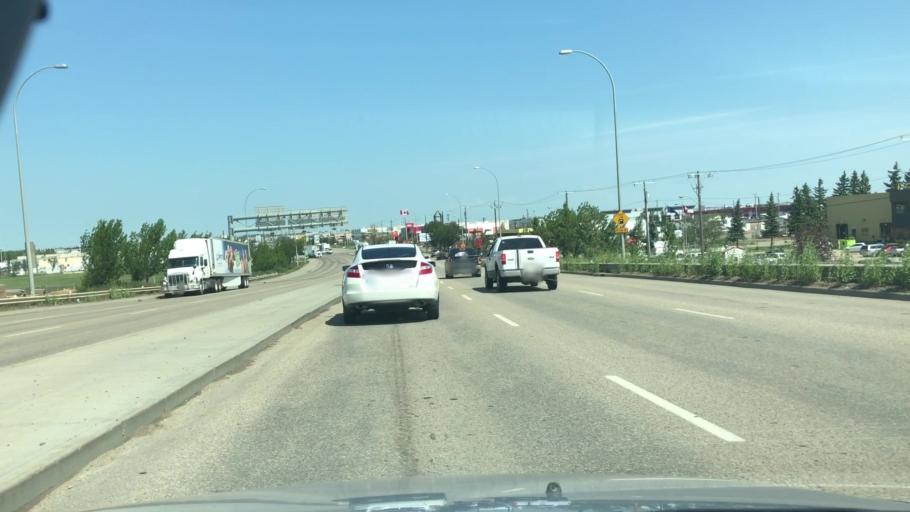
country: CA
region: Alberta
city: St. Albert
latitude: 53.5819
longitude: -113.5910
